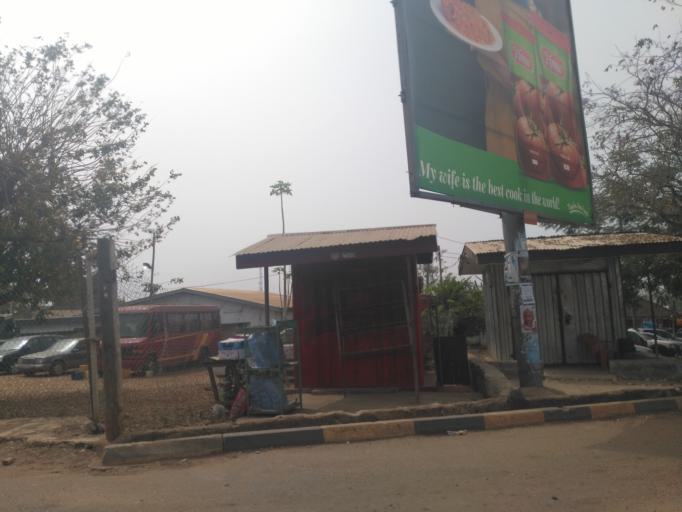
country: GH
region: Ashanti
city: Kumasi
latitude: 6.6937
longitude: -1.6354
